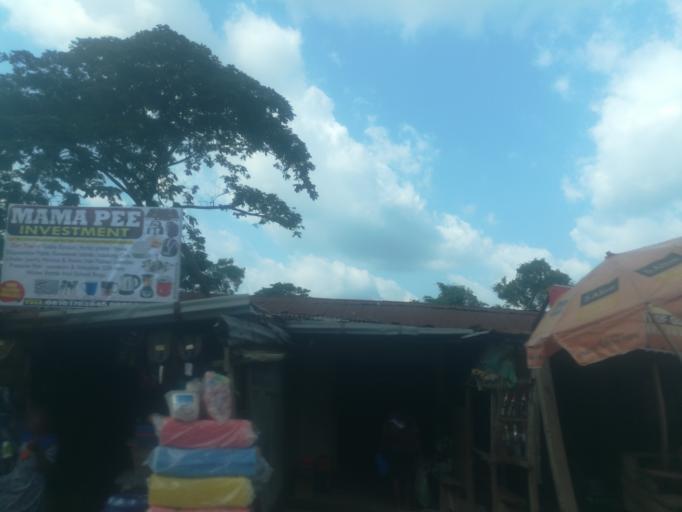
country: NG
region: Oyo
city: Moniya
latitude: 7.5130
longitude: 3.9106
